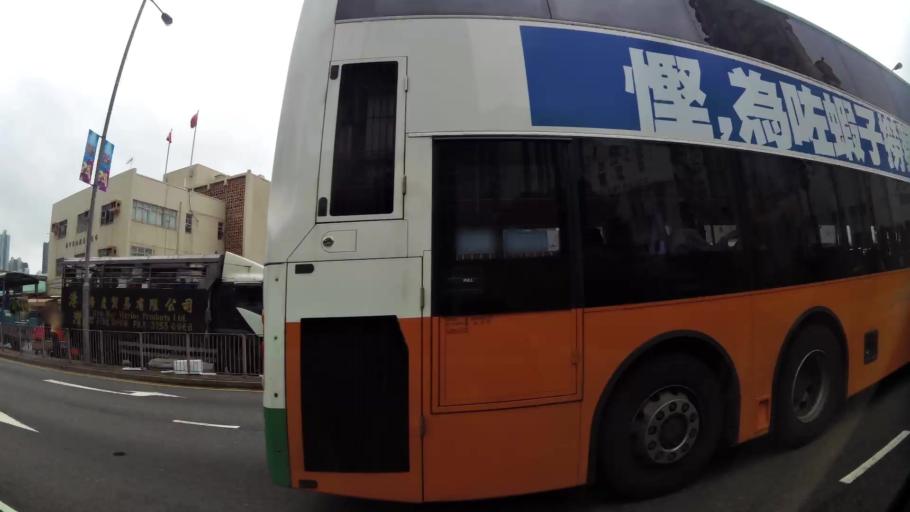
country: HK
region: Central and Western
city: Central
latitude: 22.2485
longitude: 114.1496
